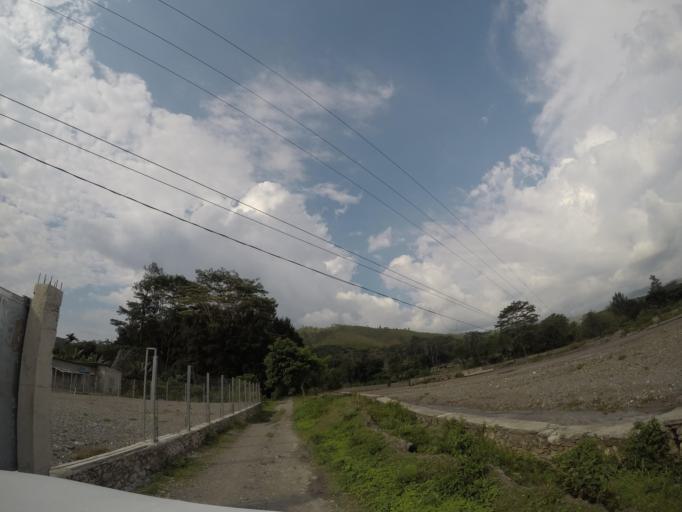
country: TL
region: Ermera
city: Gleno
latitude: -8.7137
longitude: 125.4394
